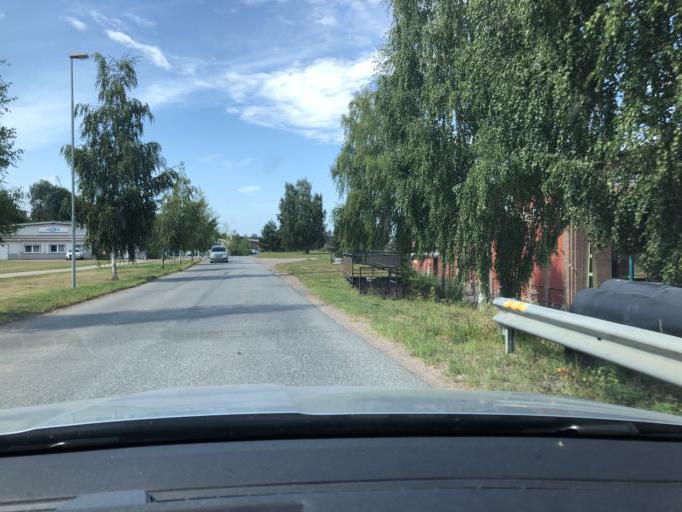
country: SE
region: Dalarna
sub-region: Avesta Kommun
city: Avesta
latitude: 60.1466
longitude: 16.1856
